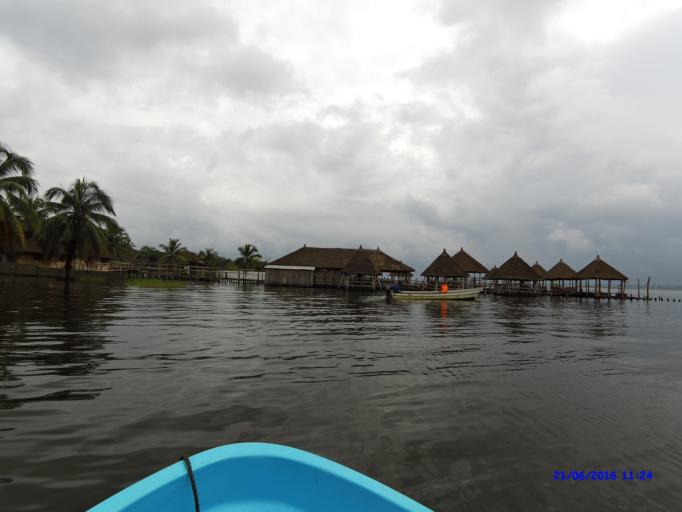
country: BJ
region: Mono
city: Come
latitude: 6.5322
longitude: 1.9709
